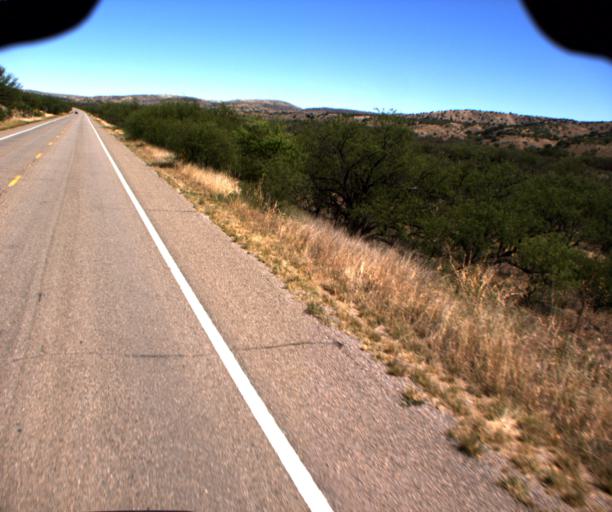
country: US
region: Arizona
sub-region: Santa Cruz County
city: Rio Rico
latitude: 31.6077
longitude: -110.7214
